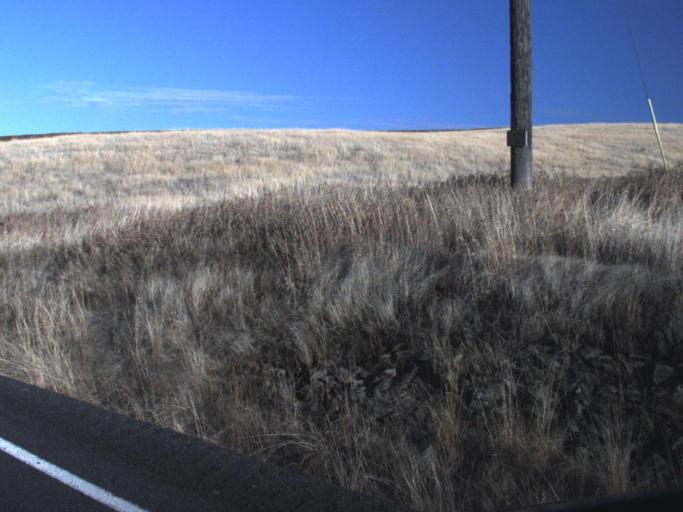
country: US
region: Washington
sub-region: Whitman County
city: Pullman
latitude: 46.7181
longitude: -117.2804
